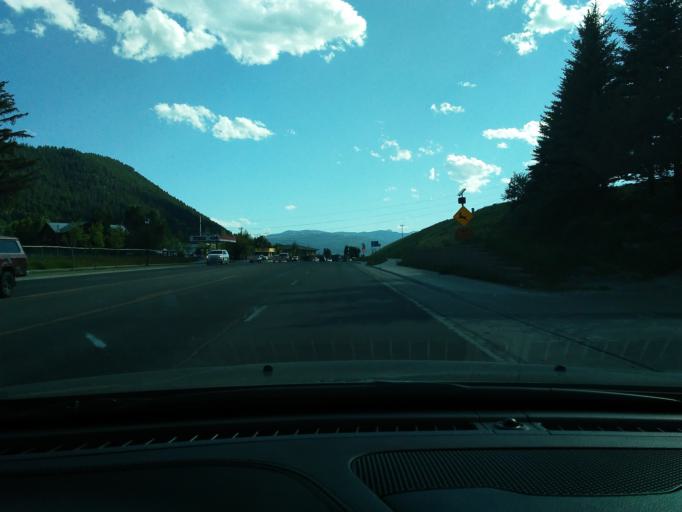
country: US
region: Wyoming
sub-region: Teton County
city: Jackson
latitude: 43.4769
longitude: -110.7720
